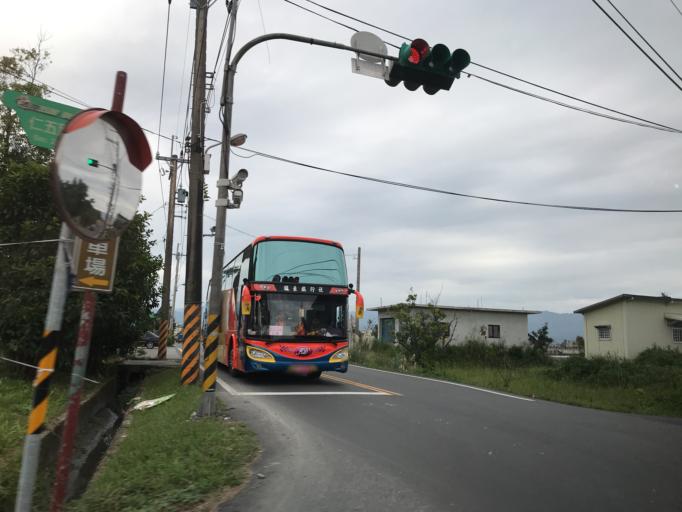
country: TW
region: Taiwan
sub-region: Yilan
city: Yilan
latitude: 24.6901
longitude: 121.7866
